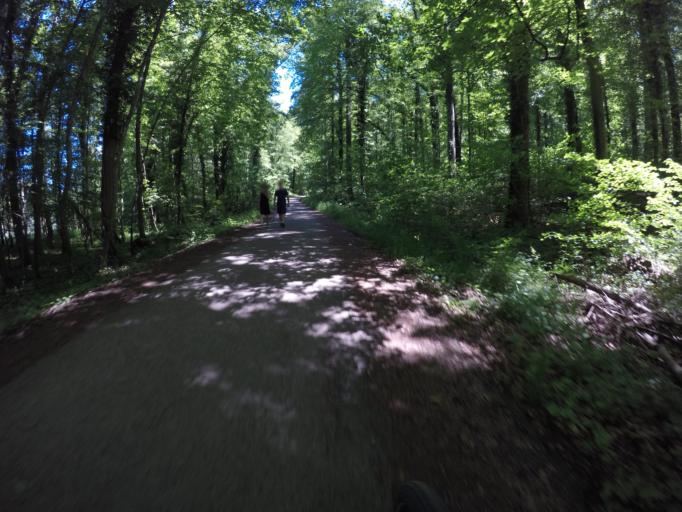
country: DE
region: Baden-Wuerttemberg
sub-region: Regierungsbezirk Stuttgart
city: Gerlingen
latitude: 48.7412
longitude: 9.0724
